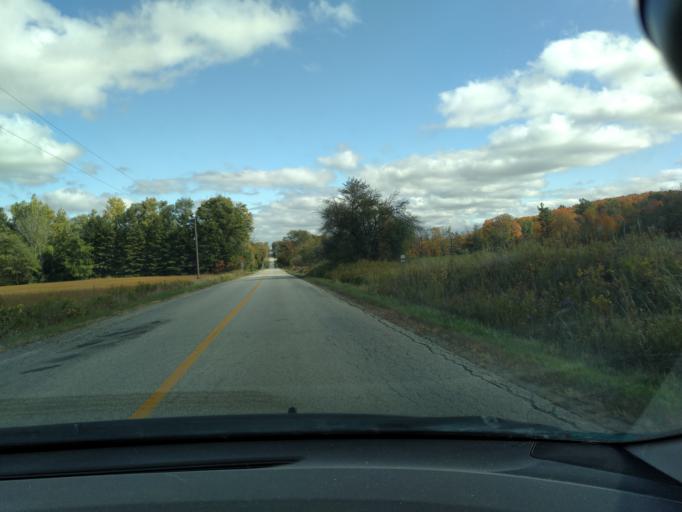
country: CA
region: Ontario
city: Bradford West Gwillimbury
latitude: 44.0811
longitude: -79.7152
